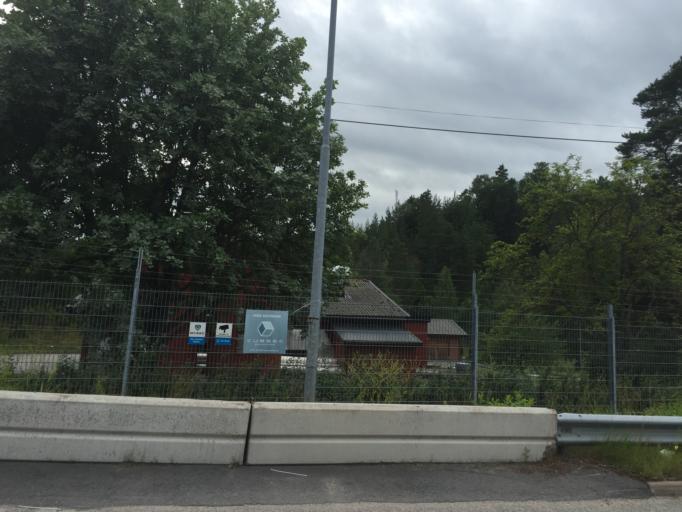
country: SE
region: Stockholm
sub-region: Botkyrka Kommun
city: Tullinge
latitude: 59.1985
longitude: 17.8849
